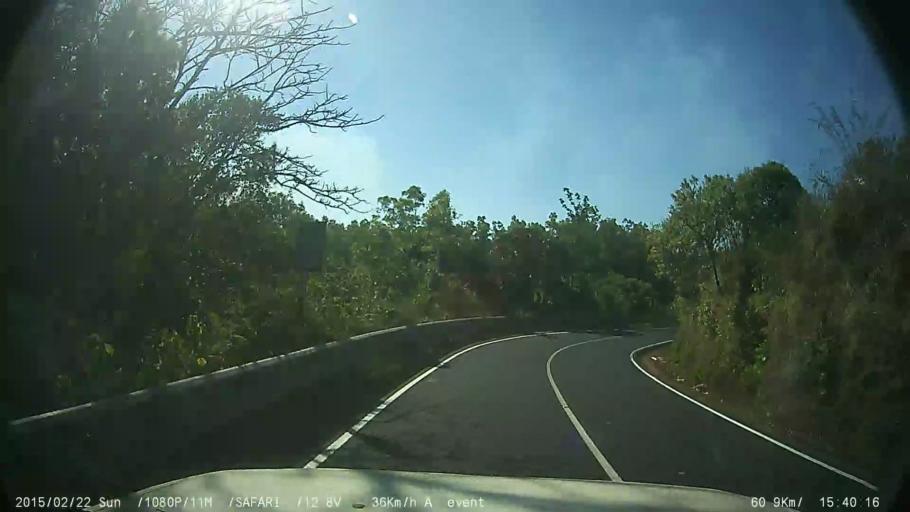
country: IN
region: Kerala
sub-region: Kottayam
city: Erattupetta
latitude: 9.5689
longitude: 76.9754
